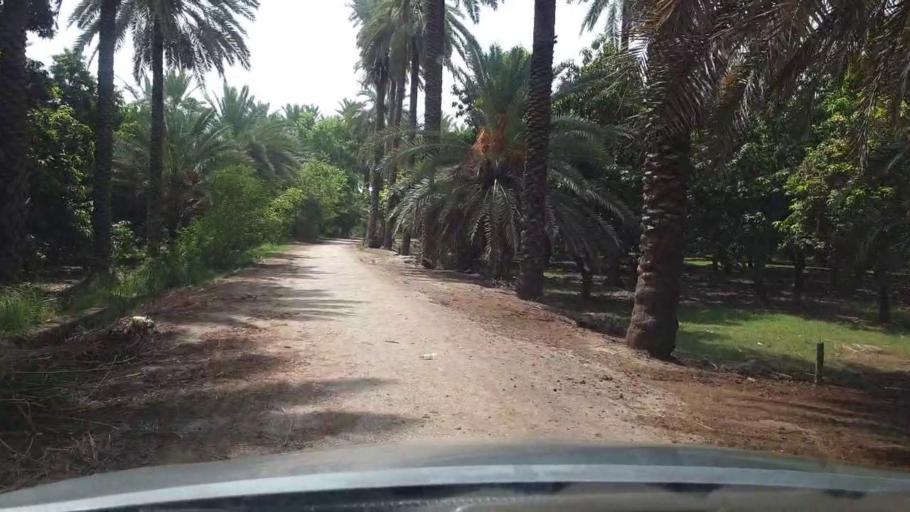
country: PK
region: Sindh
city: Pir jo Goth
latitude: 27.6174
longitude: 68.6757
